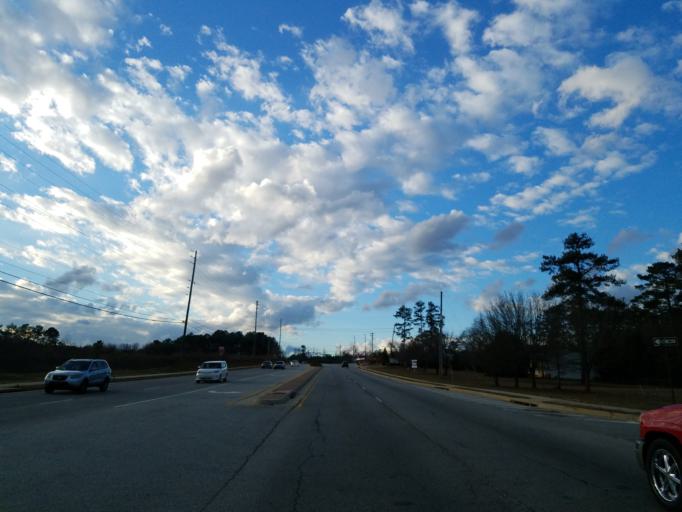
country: US
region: Georgia
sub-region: Henry County
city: McDonough
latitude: 33.4559
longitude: -84.1707
